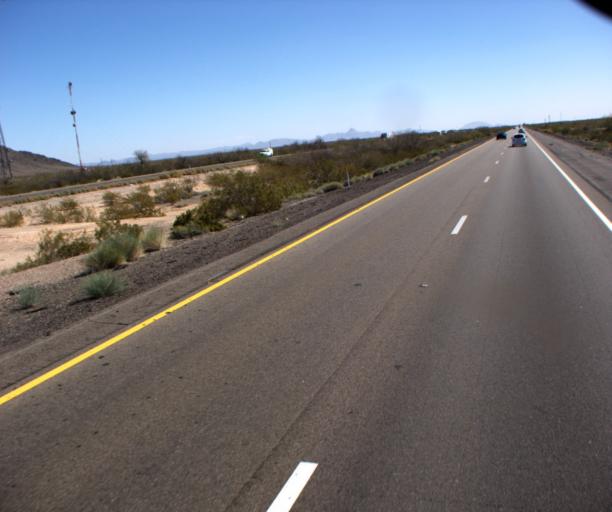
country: US
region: Arizona
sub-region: La Paz County
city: Salome
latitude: 33.5874
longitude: -113.4767
